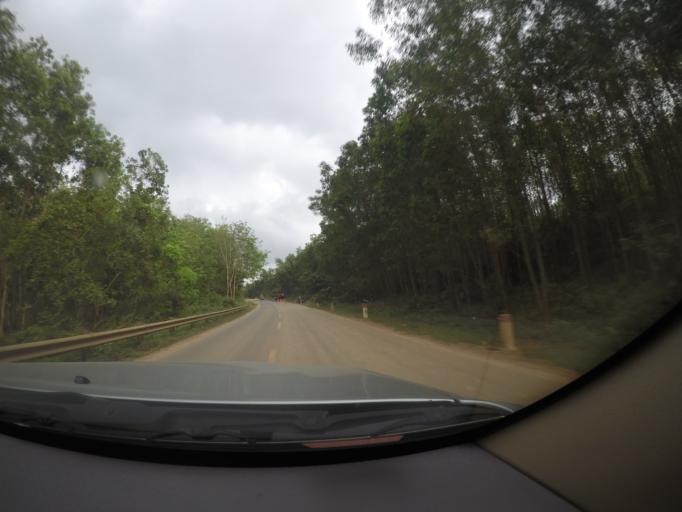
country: VN
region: Quang Tri
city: Ho Xa
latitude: 17.0404
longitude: 106.8878
